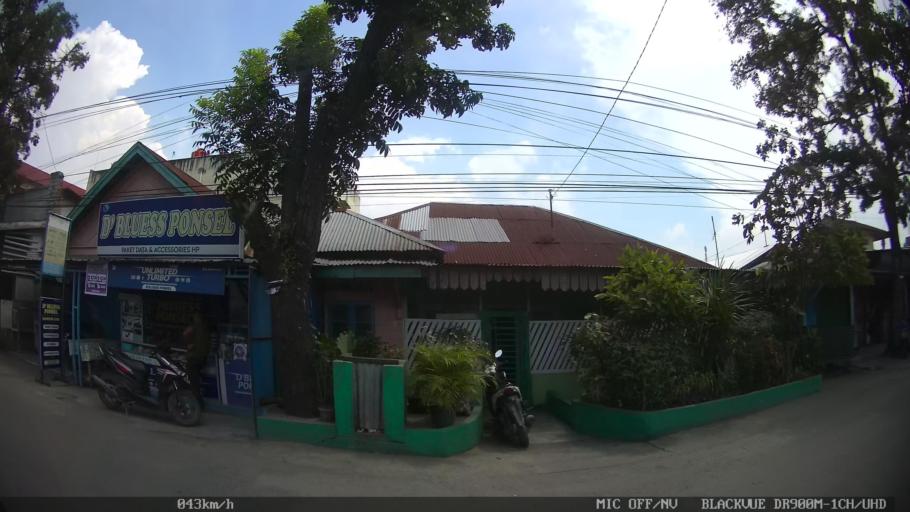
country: ID
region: North Sumatra
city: Labuhan Deli
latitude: 3.6687
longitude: 98.6800
